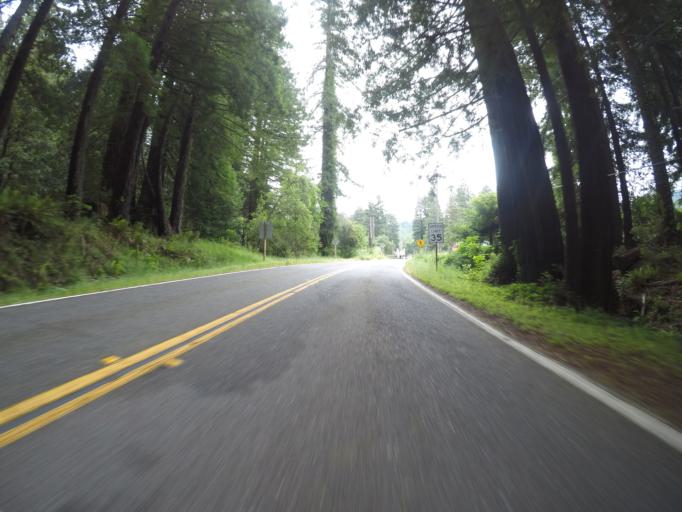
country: US
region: California
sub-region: Humboldt County
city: Rio Dell
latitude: 40.4024
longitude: -123.9508
